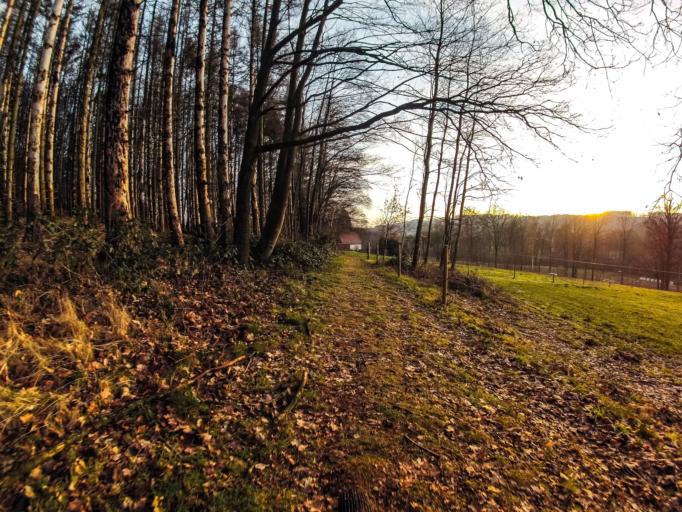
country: DE
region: North Rhine-Westphalia
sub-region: Regierungsbezirk Munster
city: Westerkappeln
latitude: 52.2908
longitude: 7.8364
